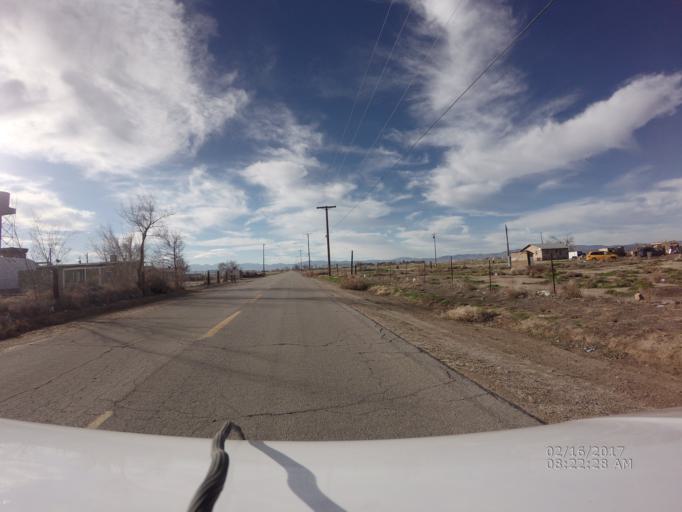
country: US
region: California
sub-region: Los Angeles County
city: Lancaster
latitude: 34.7275
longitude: -118.0054
